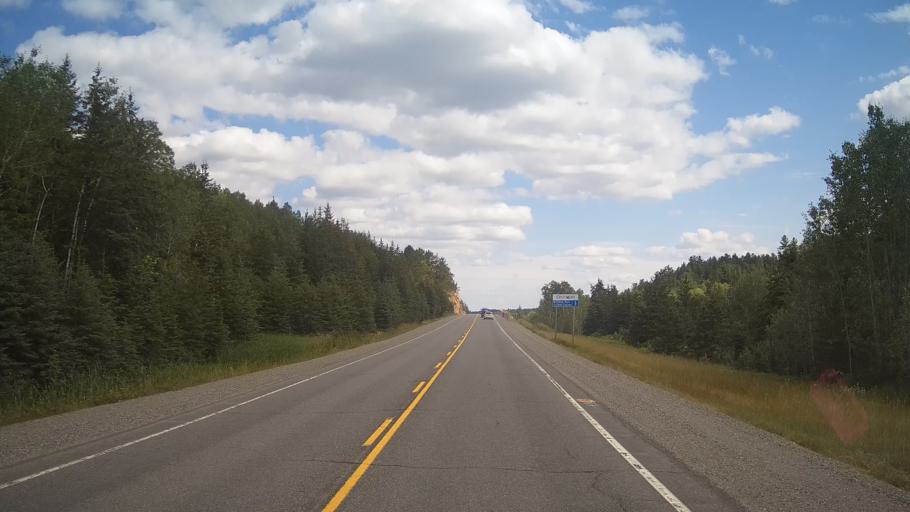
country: CA
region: Ontario
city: Greater Sudbury
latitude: 46.5002
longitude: -80.5700
